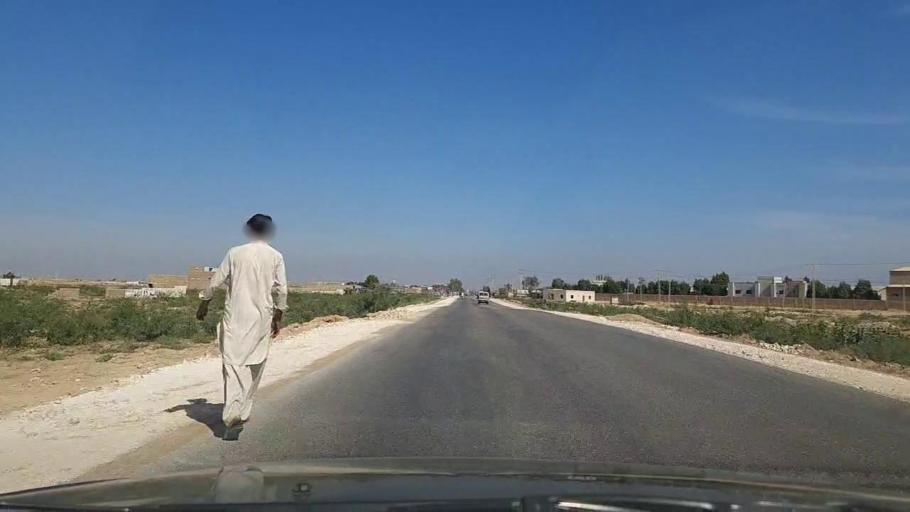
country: PK
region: Sindh
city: Kotri
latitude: 25.3364
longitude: 68.2463
